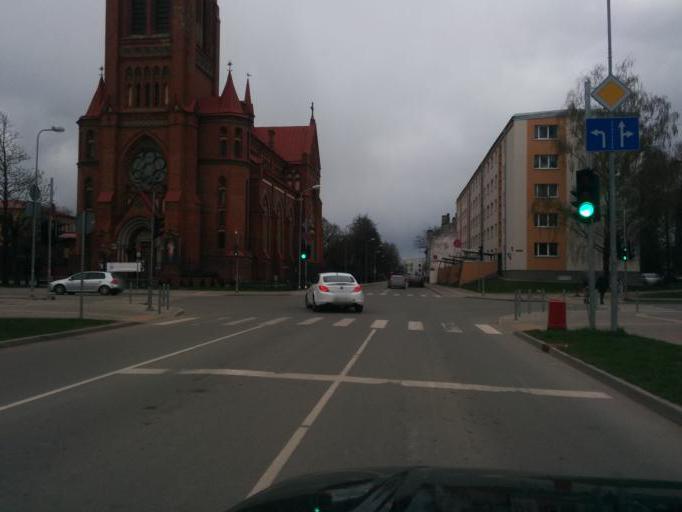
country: LV
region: Jelgava
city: Jelgava
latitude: 56.6489
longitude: 23.7262
